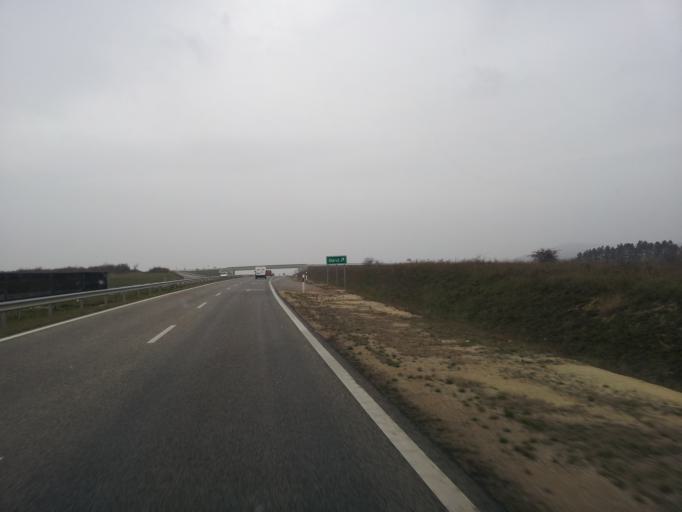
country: HU
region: Veszprem
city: Herend
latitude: 47.1172
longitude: 17.8072
